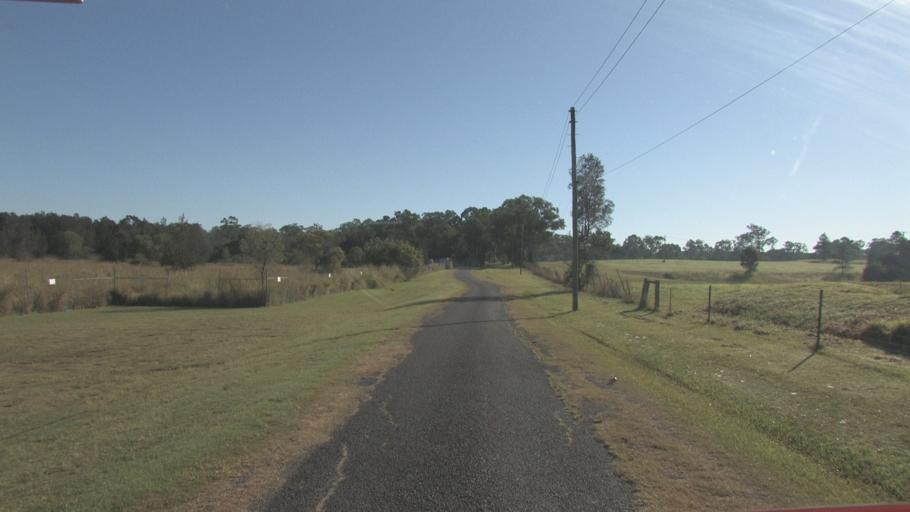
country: AU
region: Queensland
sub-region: Gold Coast
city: Yatala
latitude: -27.6933
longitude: 153.2796
